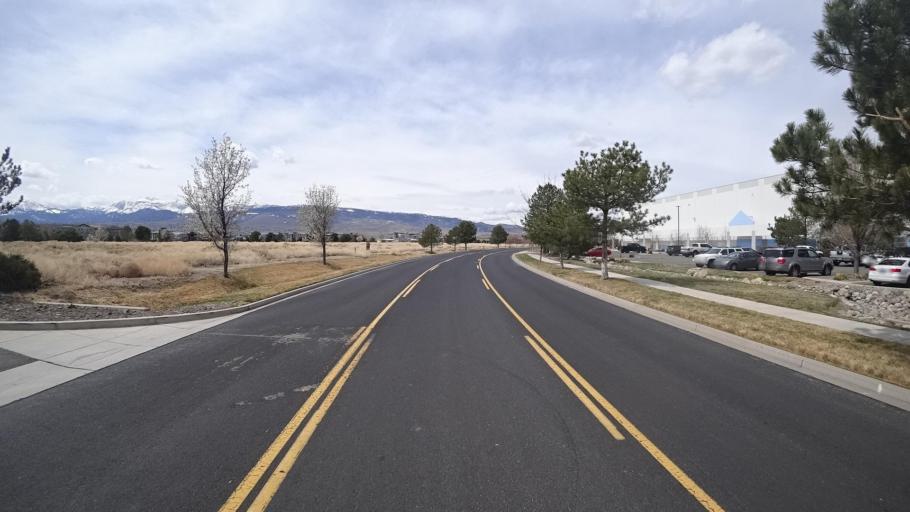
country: US
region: Nevada
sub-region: Washoe County
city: Sparks
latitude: 39.4443
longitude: -119.7532
